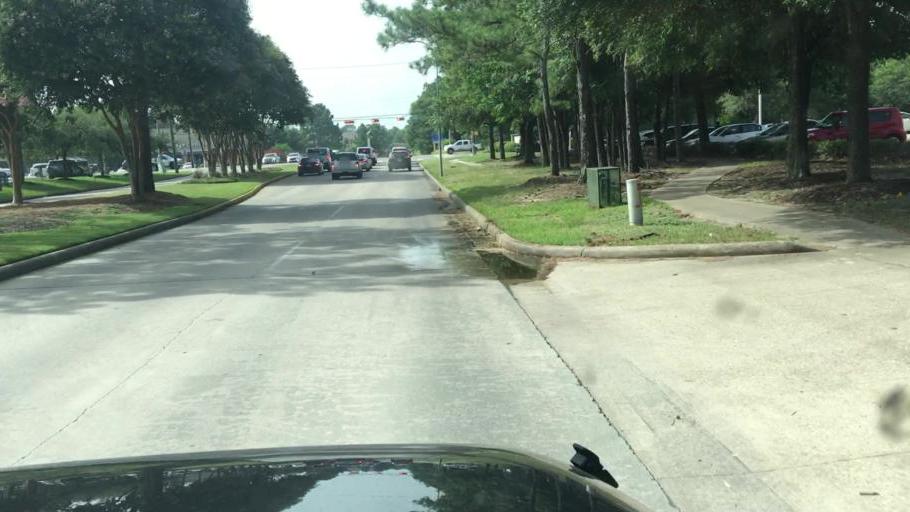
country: US
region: Texas
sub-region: Harris County
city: Atascocita
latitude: 29.9875
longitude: -95.1920
